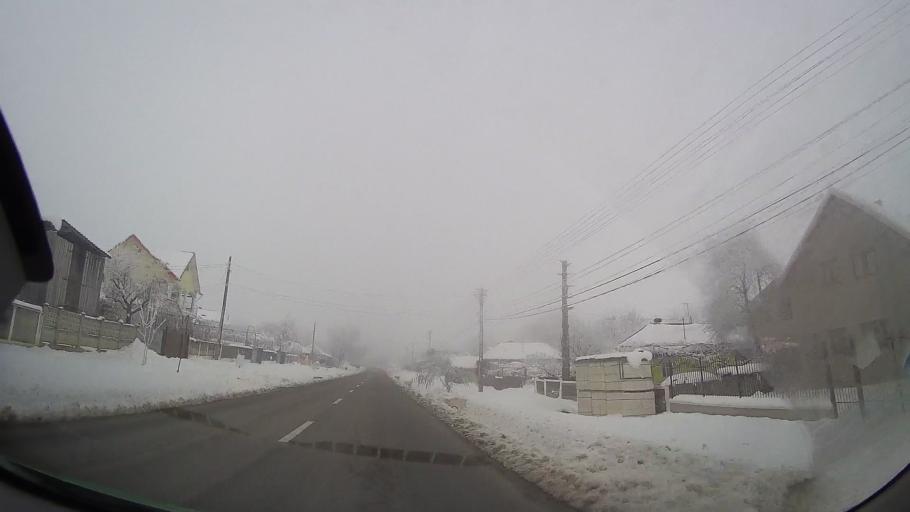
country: RO
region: Iasi
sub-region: Comuna Halaucesti
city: Halaucesti
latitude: 47.0967
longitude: 26.8191
